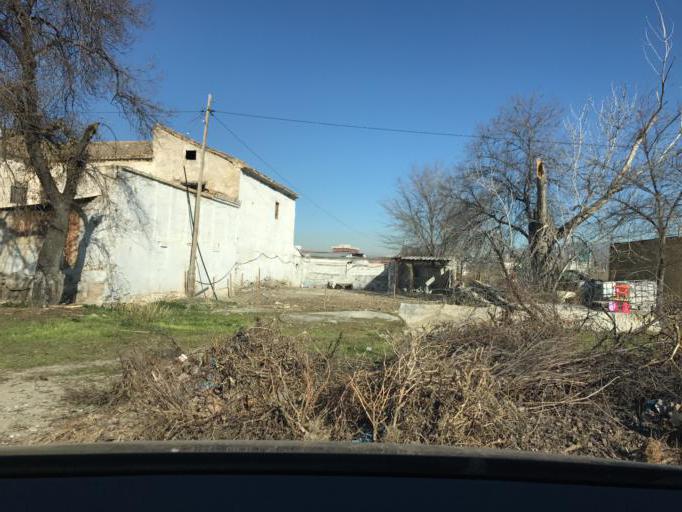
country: ES
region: Andalusia
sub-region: Provincia de Granada
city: Armilla
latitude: 37.1442
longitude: -3.5981
